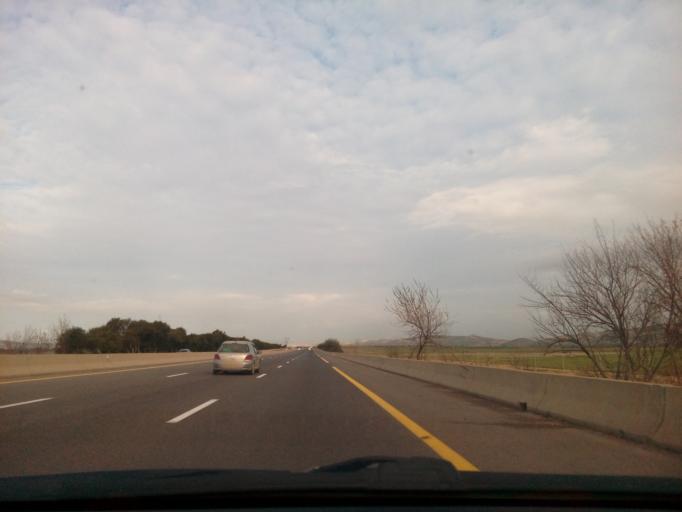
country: DZ
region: Mostaganem
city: Mostaganem
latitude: 35.6904
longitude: 0.1685
